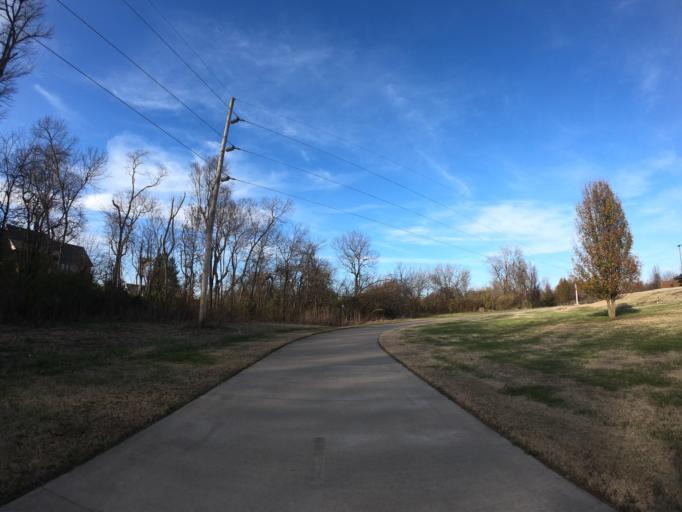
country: US
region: Arkansas
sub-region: Benton County
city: Lowell
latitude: 36.2865
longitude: -94.1661
